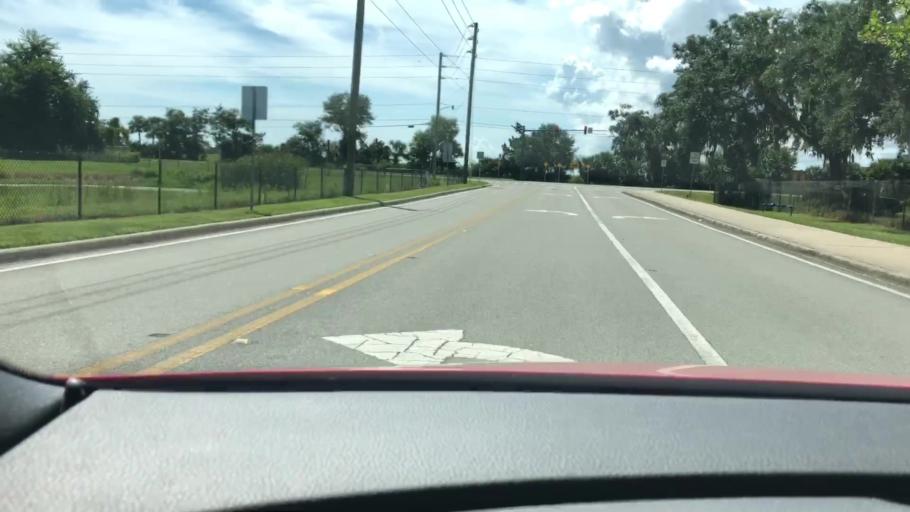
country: US
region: Florida
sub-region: Volusia County
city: New Smyrna Beach
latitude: 29.0036
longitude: -80.9221
